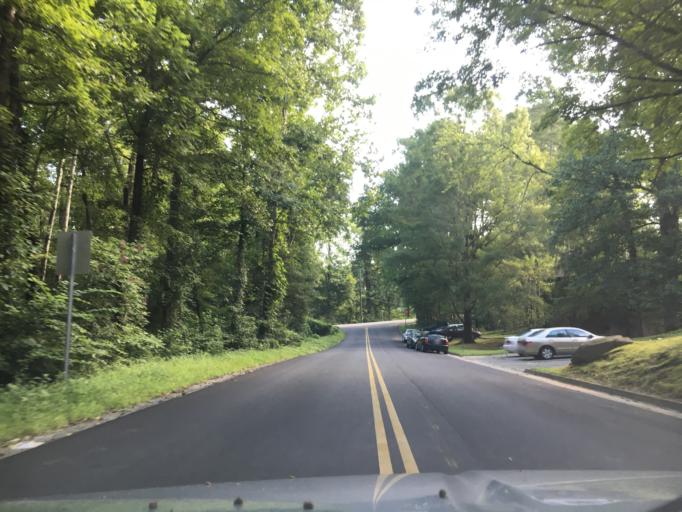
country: US
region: Virginia
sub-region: Halifax County
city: South Boston
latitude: 36.7091
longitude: -78.9132
